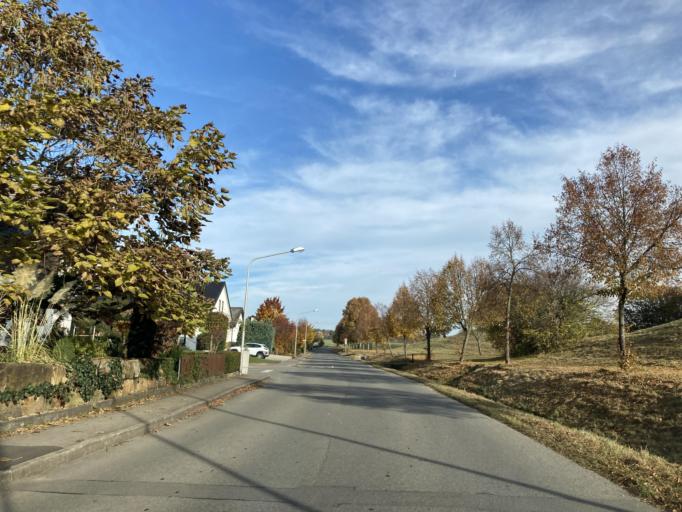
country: DE
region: Baden-Wuerttemberg
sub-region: Tuebingen Region
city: Bodelshausen
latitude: 48.3983
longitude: 8.9767
